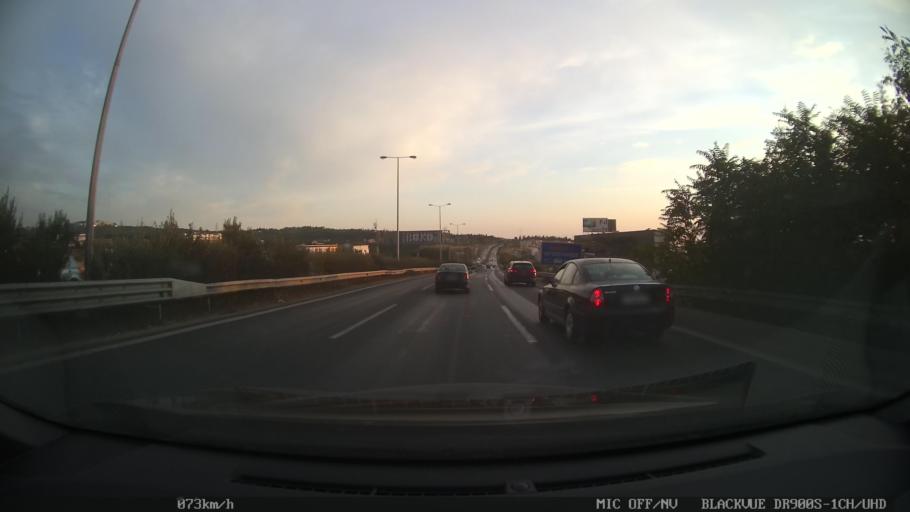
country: GR
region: Central Macedonia
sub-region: Nomos Thessalonikis
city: Pylaia
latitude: 40.6098
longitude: 22.9999
